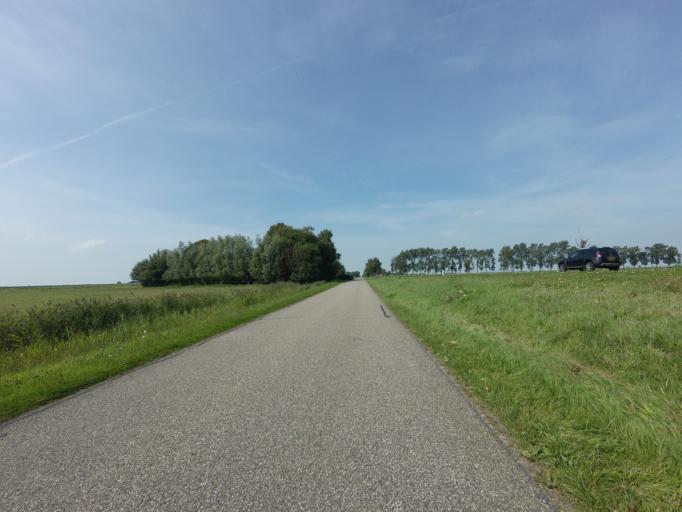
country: NL
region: Friesland
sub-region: Gemeente Skarsterlan
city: Sint Nicolaasga
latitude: 52.9187
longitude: 5.6872
